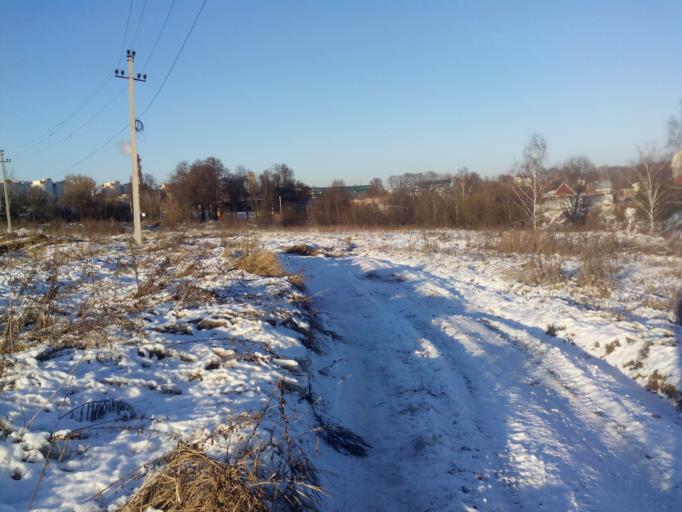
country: RU
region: Moskovskaya
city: Yakovlevskoye
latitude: 55.4967
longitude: 37.9530
